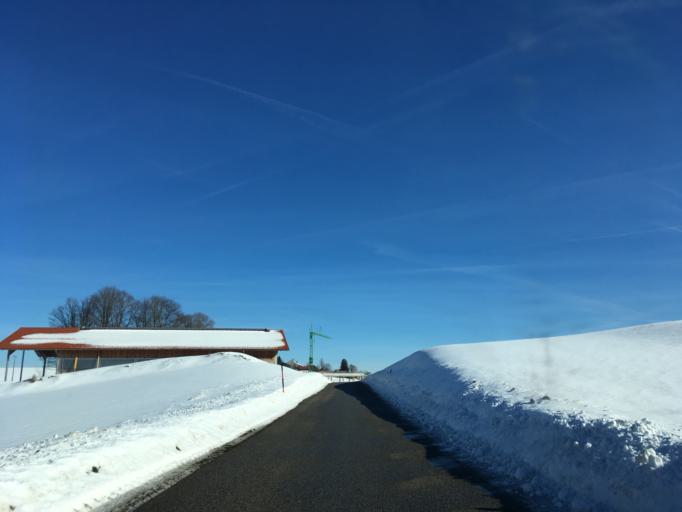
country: DE
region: Bavaria
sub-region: Upper Bavaria
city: Frasdorf
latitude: 47.8057
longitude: 12.3108
